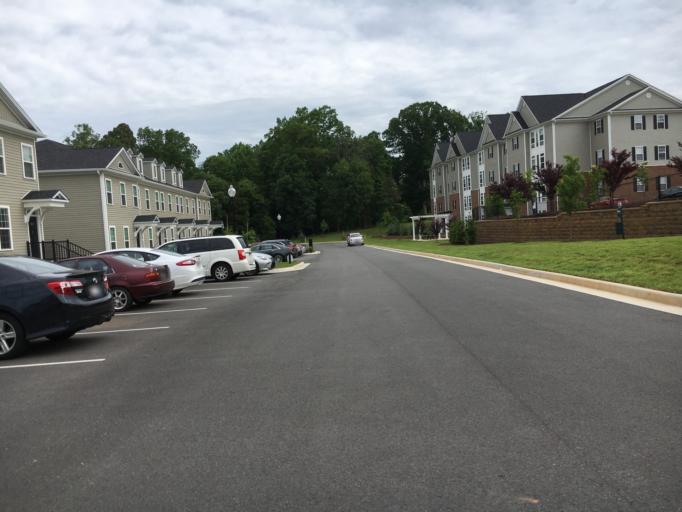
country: US
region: Virginia
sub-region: Bedford County
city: Forest
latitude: 37.3694
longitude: -79.2575
